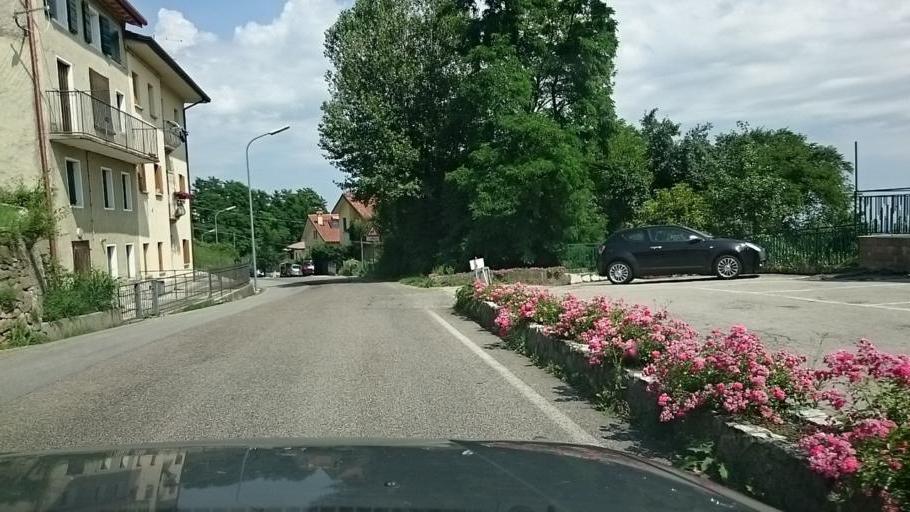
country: IT
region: Veneto
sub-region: Provincia di Vicenza
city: Conco
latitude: 45.7737
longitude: 11.6145
